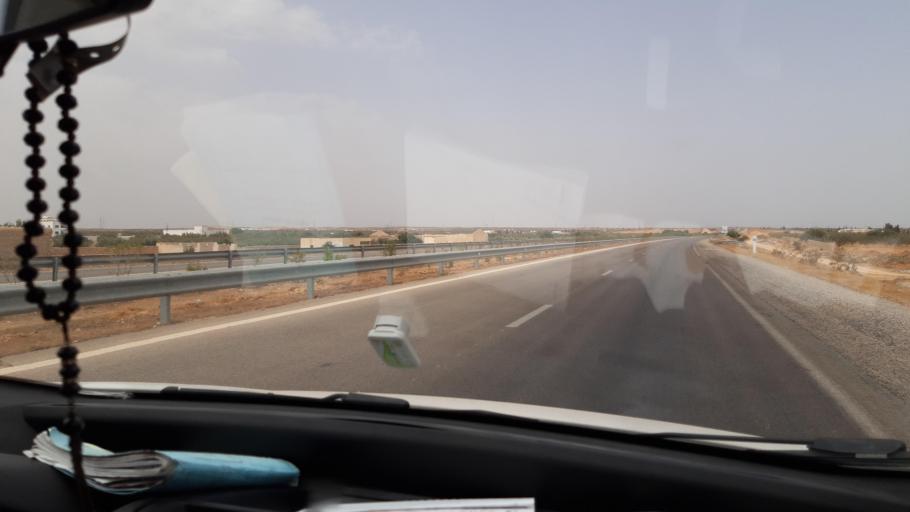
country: TN
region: Safaqis
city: Sfax
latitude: 34.8767
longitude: 10.6997
